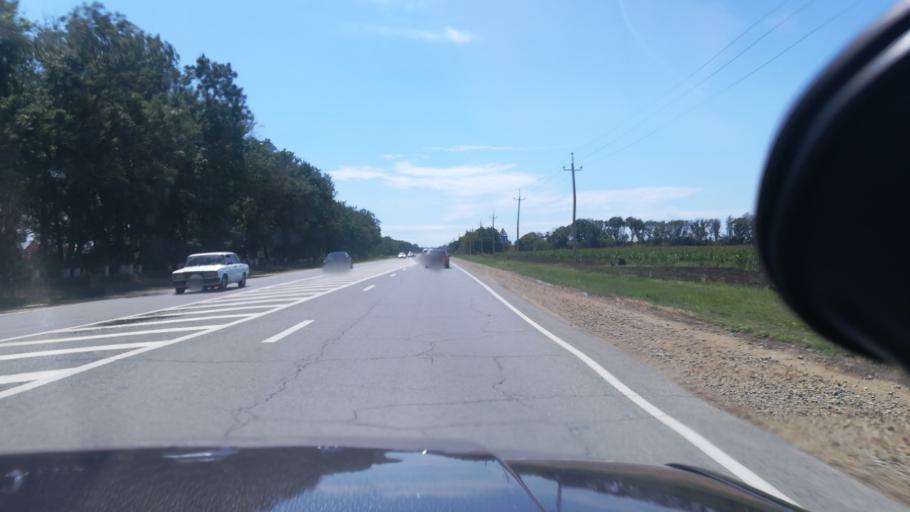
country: RU
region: Krasnodarskiy
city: Tsibanobalka
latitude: 44.9965
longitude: 37.3213
